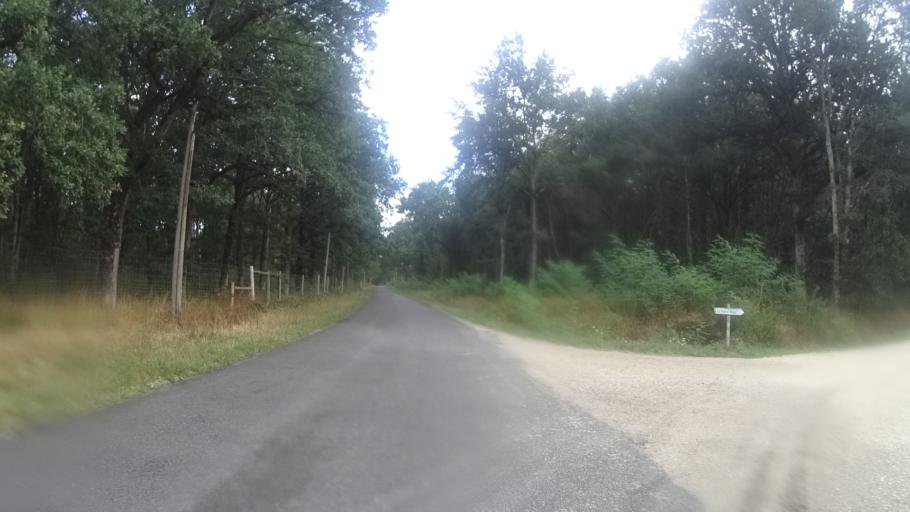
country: FR
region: Centre
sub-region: Departement du Loiret
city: Chateauneuf-sur-Loire
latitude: 47.9025
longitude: 2.2109
